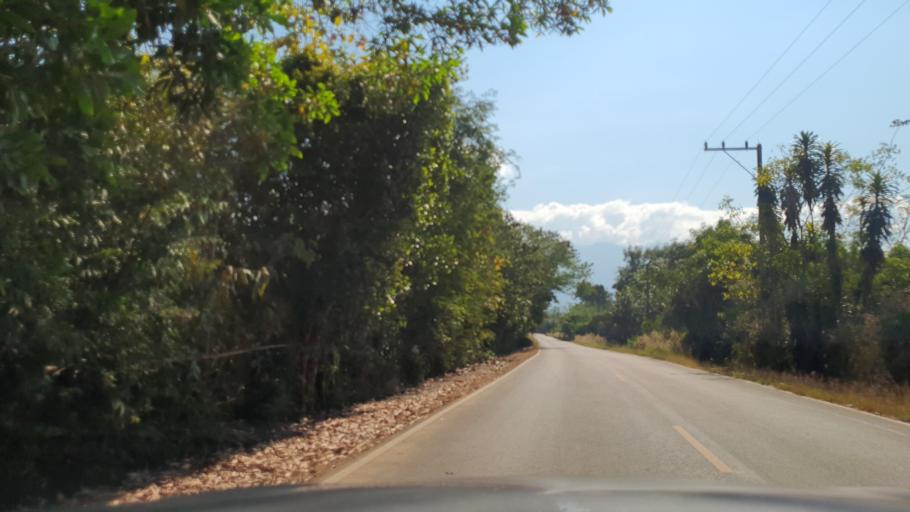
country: TH
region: Nan
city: Pua
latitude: 19.1480
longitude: 100.9169
